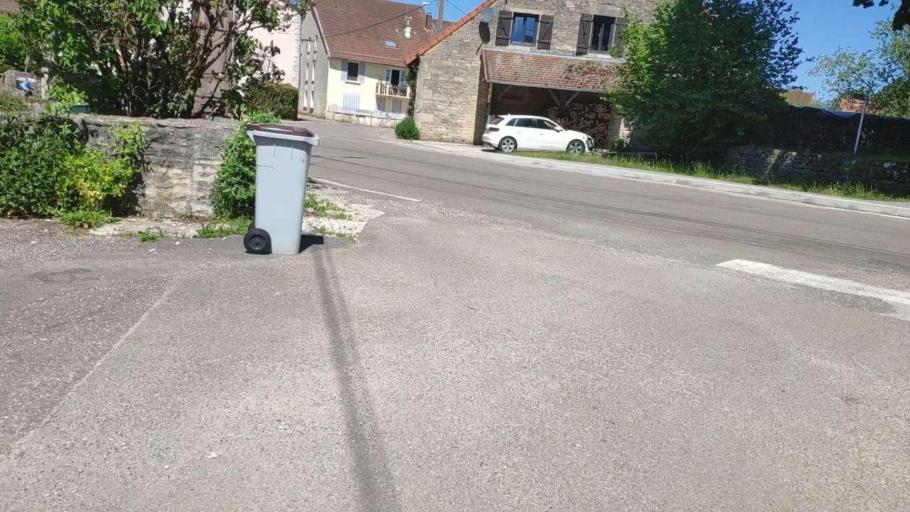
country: FR
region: Franche-Comte
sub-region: Departement du Jura
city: Poligny
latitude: 46.7350
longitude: 5.6985
